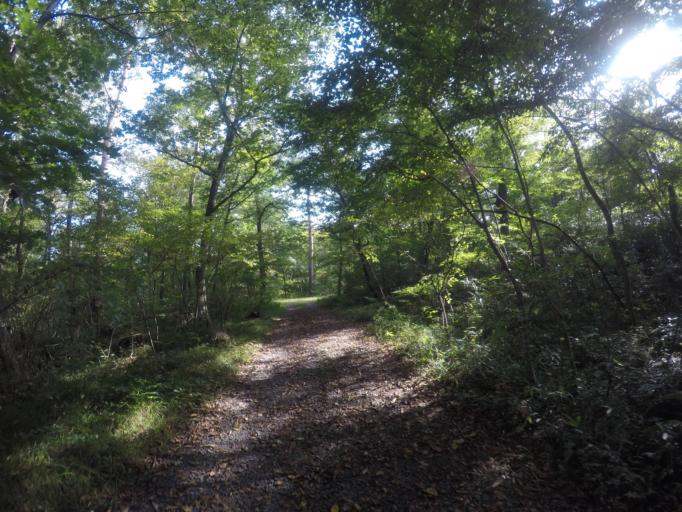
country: JP
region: Fukushima
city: Fukushima-shi
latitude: 37.7055
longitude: 140.3493
